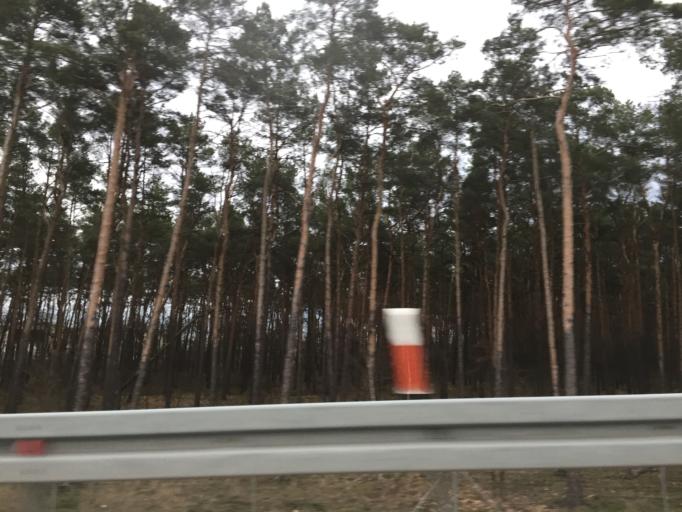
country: PL
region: Kujawsko-Pomorskie
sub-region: Bydgoszcz
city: Bydgoszcz
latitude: 53.0933
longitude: 18.0094
